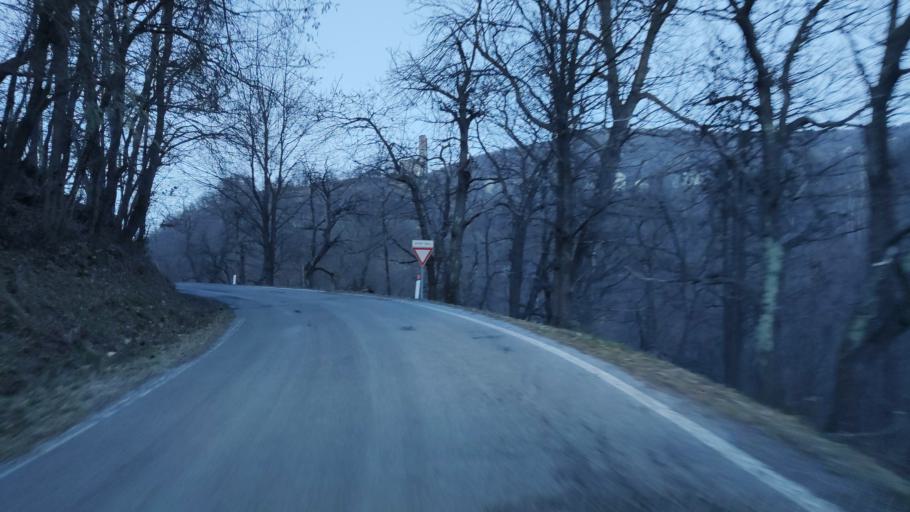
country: IT
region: Piedmont
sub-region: Provincia di Cuneo
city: Viola
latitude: 44.2915
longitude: 7.9775
